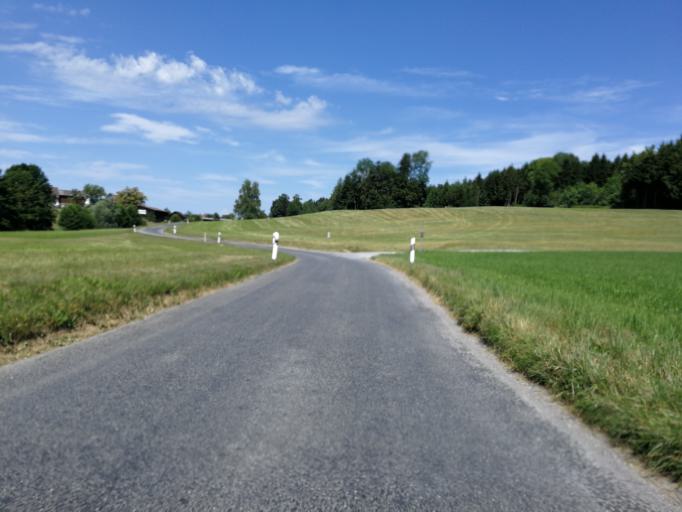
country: CH
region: Zurich
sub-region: Bezirk Hinwil
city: Durnten
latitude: 47.2791
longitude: 8.8342
